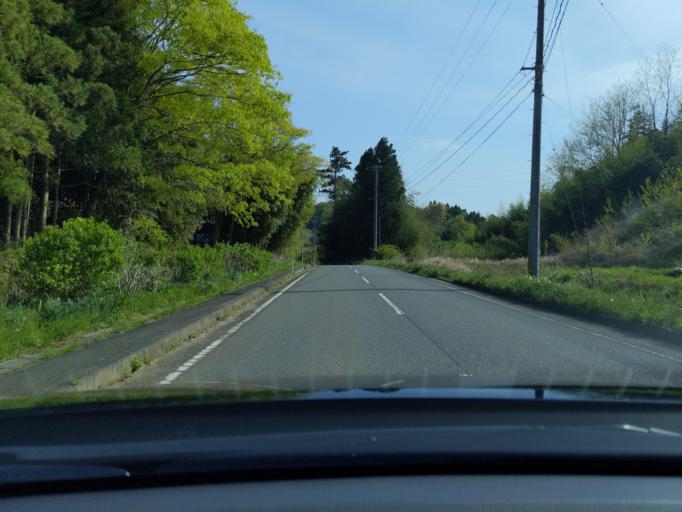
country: JP
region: Fukushima
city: Sukagawa
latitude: 37.3009
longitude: 140.4246
